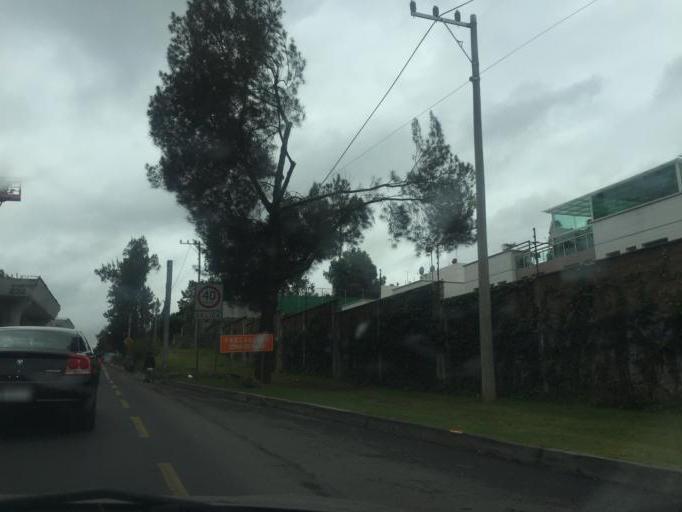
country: MX
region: Mexico City
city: Tlalpan
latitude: 19.2594
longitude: -99.1636
